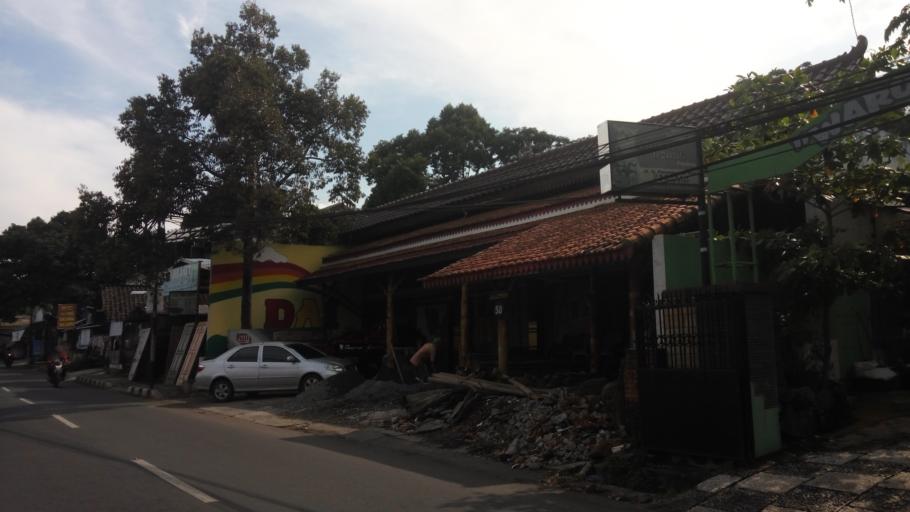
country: ID
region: Central Java
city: Ungaran
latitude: -7.1408
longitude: 110.4124
